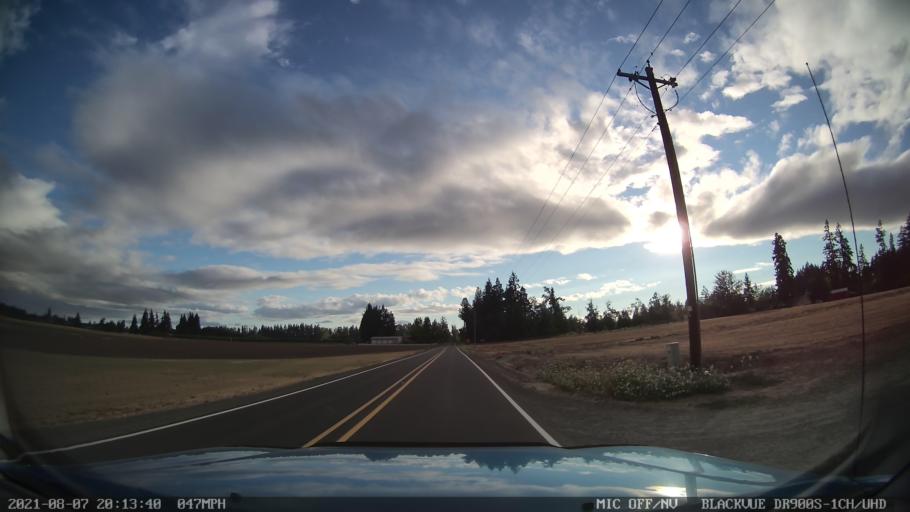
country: US
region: Oregon
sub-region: Marion County
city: Hayesville
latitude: 44.9566
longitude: -122.9272
